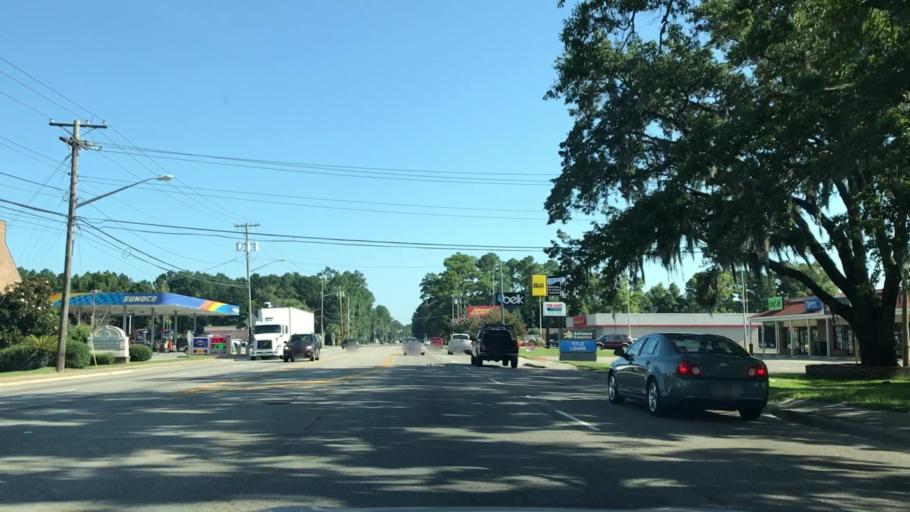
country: US
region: South Carolina
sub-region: Georgetown County
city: Georgetown
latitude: 33.3904
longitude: -79.2890
